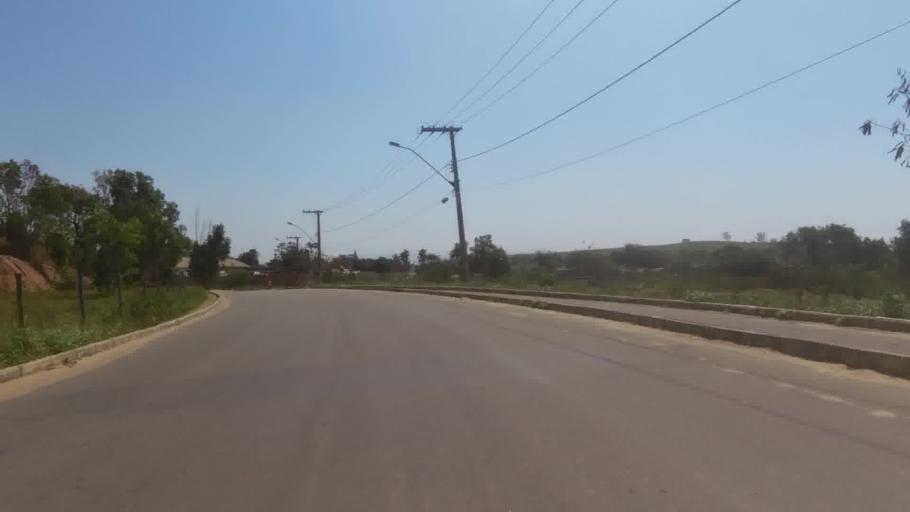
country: BR
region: Espirito Santo
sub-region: Itapemirim
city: Itapemirim
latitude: -21.0119
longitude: -40.8263
